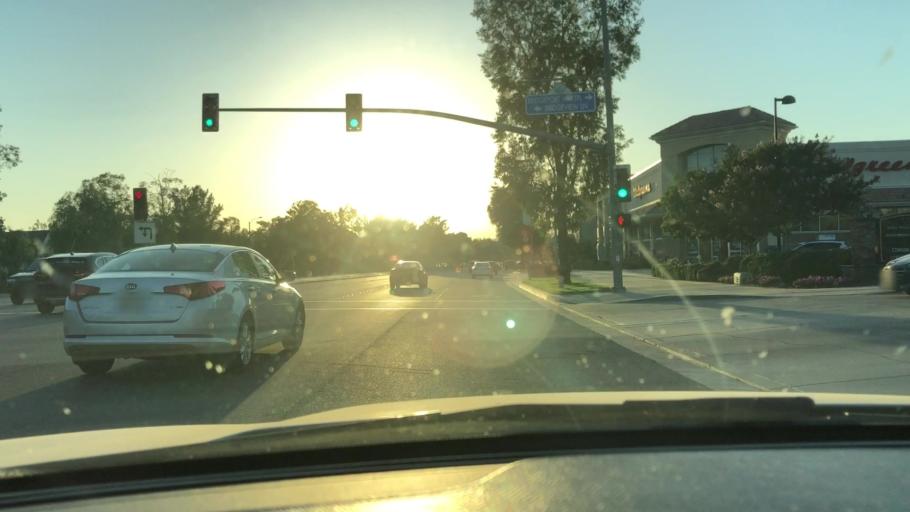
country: US
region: California
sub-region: Los Angeles County
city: Santa Clarita
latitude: 34.4294
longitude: -118.5540
